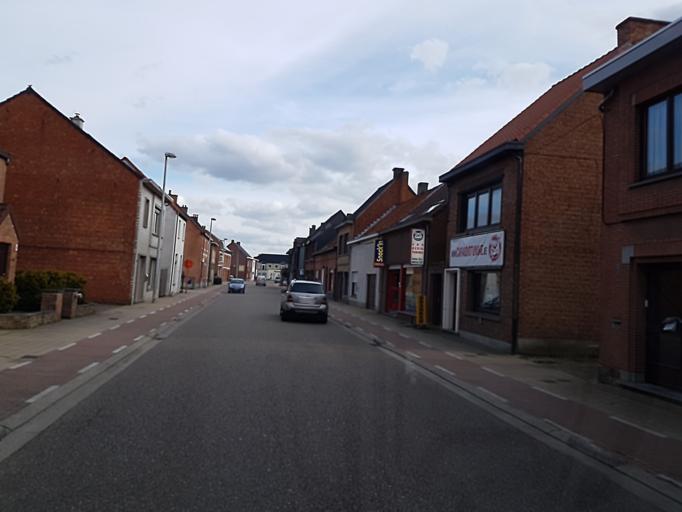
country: BE
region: Flanders
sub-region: Provincie Oost-Vlaanderen
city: Sint-Niklaas
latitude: 51.1870
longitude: 4.1833
